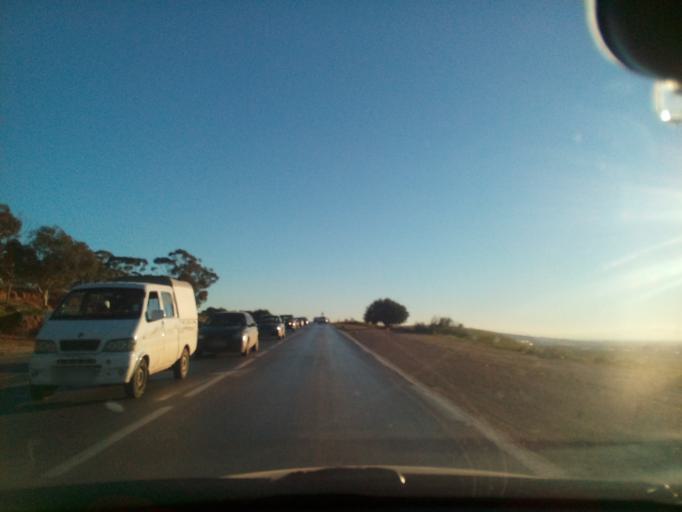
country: DZ
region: Mostaganem
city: Mostaganem
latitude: 35.7670
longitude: 0.2001
